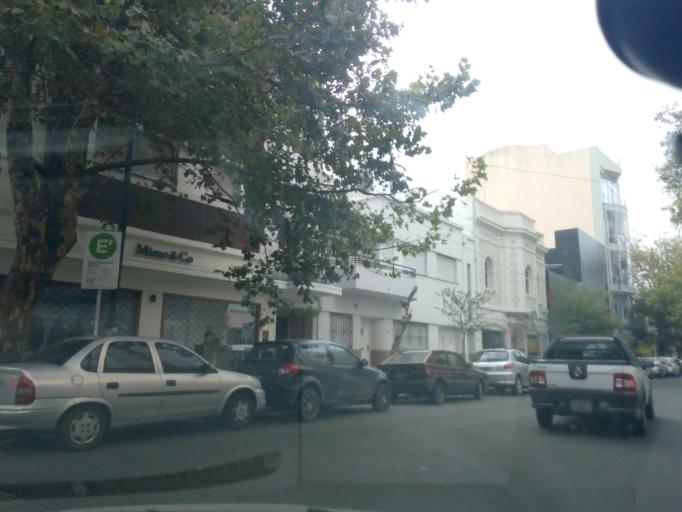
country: AR
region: Buenos Aires
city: Mar del Plata
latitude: -37.9977
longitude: -57.5524
